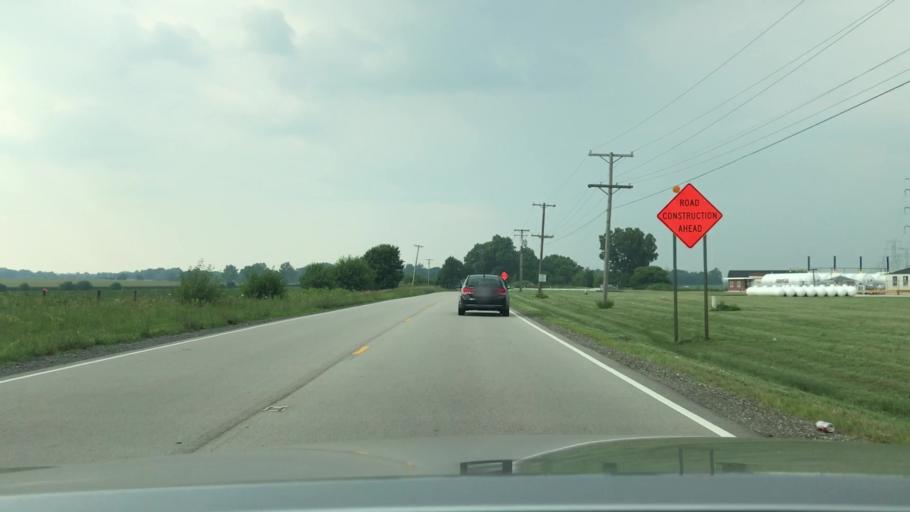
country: US
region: Illinois
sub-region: Will County
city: Plainfield
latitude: 41.6561
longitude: -88.2340
